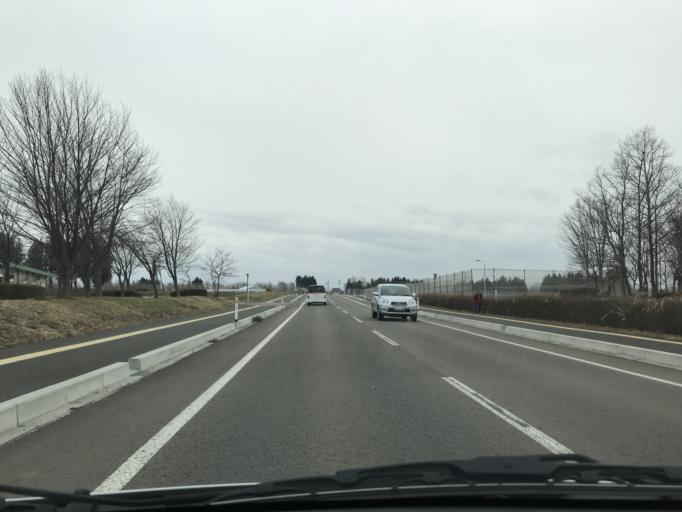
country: JP
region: Iwate
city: Hanamaki
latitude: 39.3555
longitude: 141.1070
